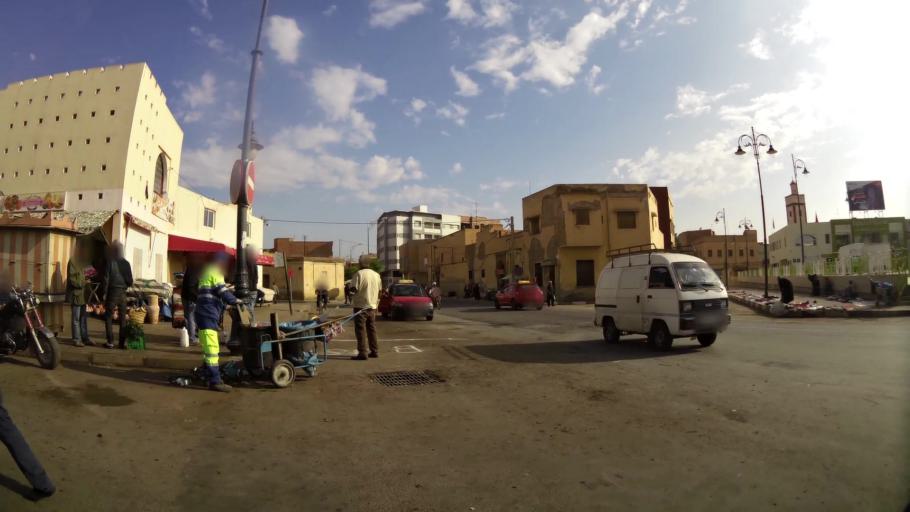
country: MA
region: Oriental
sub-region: Oujda-Angad
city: Oujda
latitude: 34.6818
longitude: -1.9092
